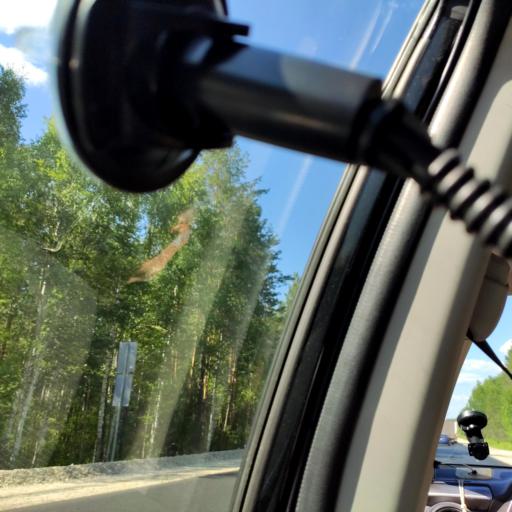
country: RU
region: Mariy-El
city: Suslonger
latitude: 56.2622
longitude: 48.2326
